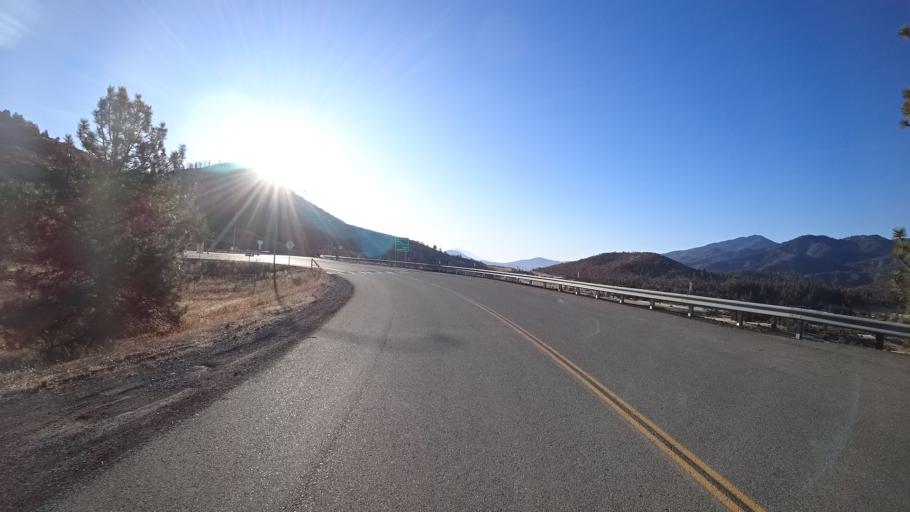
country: US
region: Oregon
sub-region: Jackson County
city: Ashland
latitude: 41.9930
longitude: -122.6113
